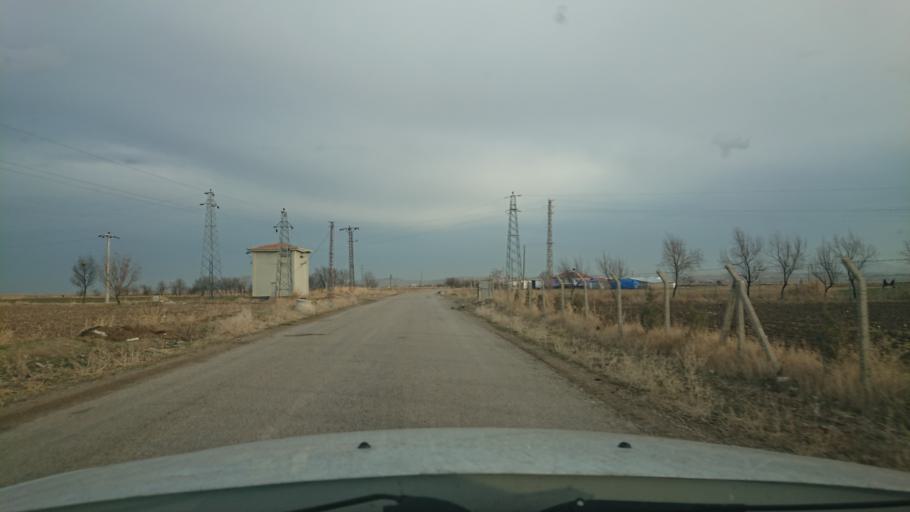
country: TR
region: Aksaray
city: Yesilova
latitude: 38.4271
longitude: 33.8351
